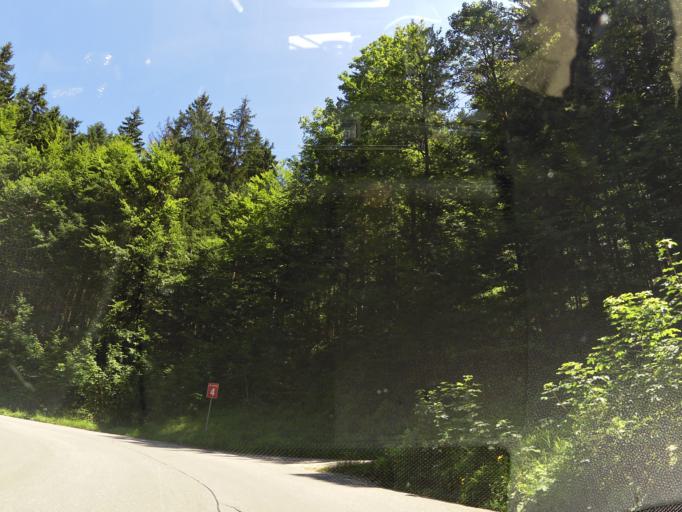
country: AT
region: Tyrol
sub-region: Politischer Bezirk Kitzbuhel
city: Waidring
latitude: 47.6606
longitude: 12.5586
